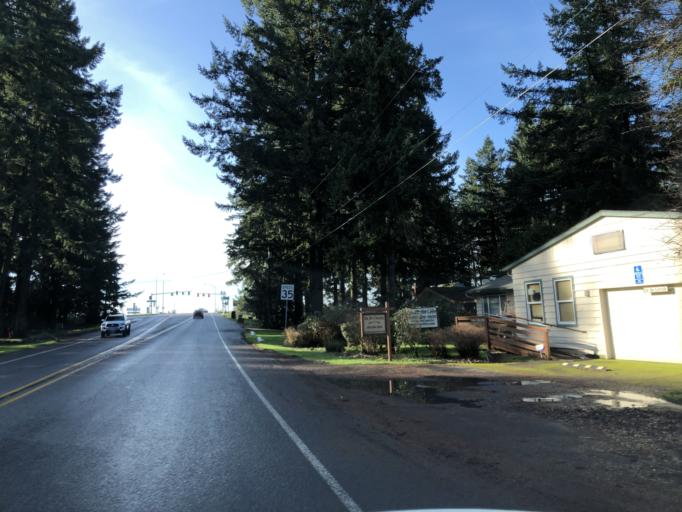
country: US
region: Oregon
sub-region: Washington County
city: Durham
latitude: 45.4097
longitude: -122.7409
